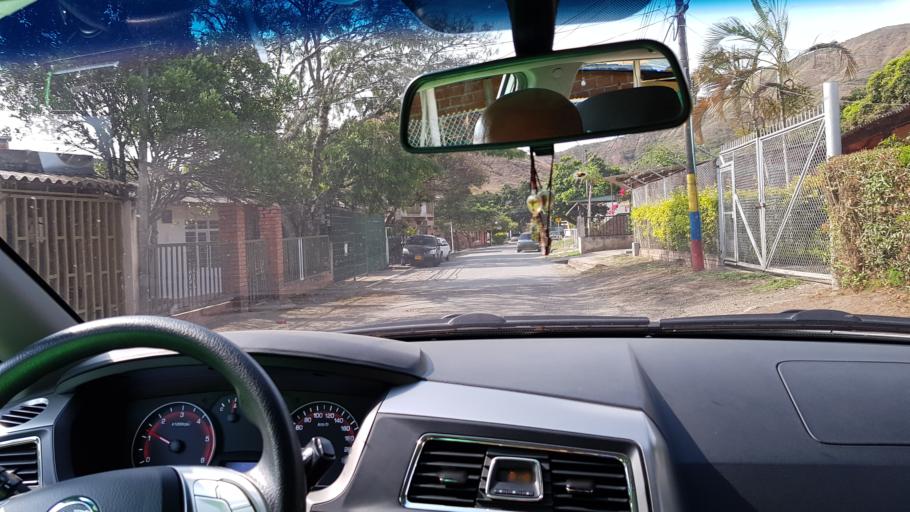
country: CO
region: Valle del Cauca
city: Yumbo
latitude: 3.6372
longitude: -76.4833
